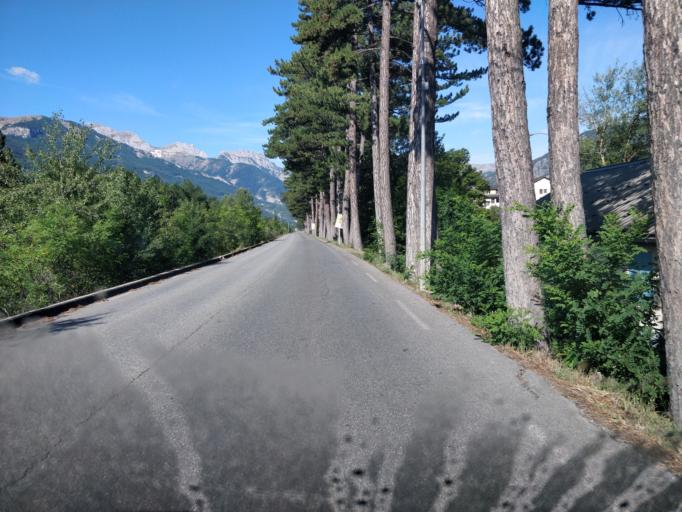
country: FR
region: Provence-Alpes-Cote d'Azur
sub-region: Departement des Alpes-de-Haute-Provence
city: Barcelonnette
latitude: 44.3864
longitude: 6.6399
